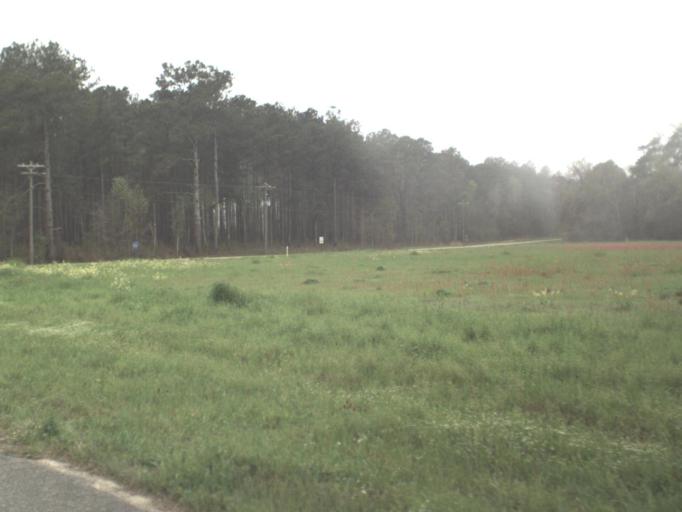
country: US
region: Florida
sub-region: Gadsden County
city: Gretna
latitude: 30.5232
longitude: -84.6903
